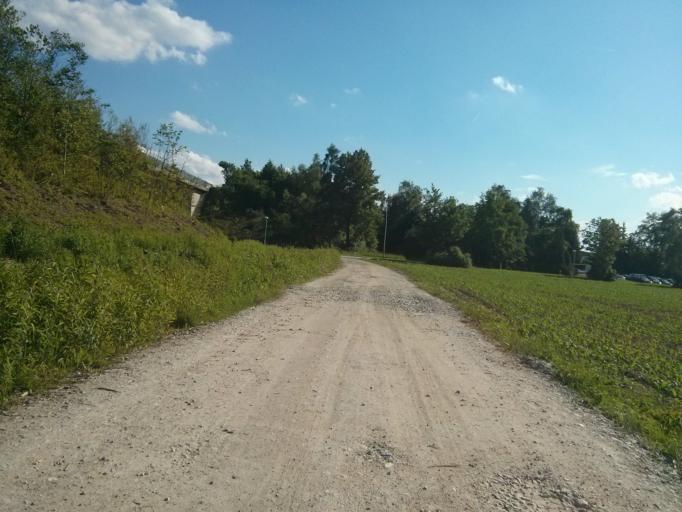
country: DE
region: Bavaria
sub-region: Lower Bavaria
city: Deggendorf
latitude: 48.8239
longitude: 12.9441
